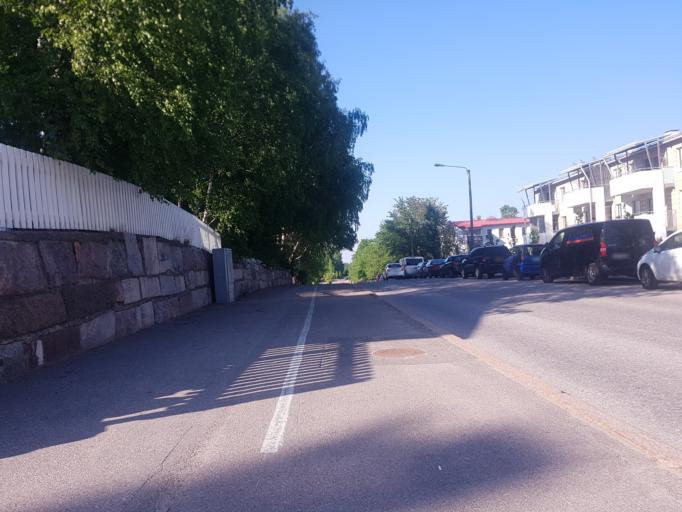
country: FI
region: Uusimaa
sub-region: Helsinki
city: Vantaa
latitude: 60.2628
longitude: 25.0115
